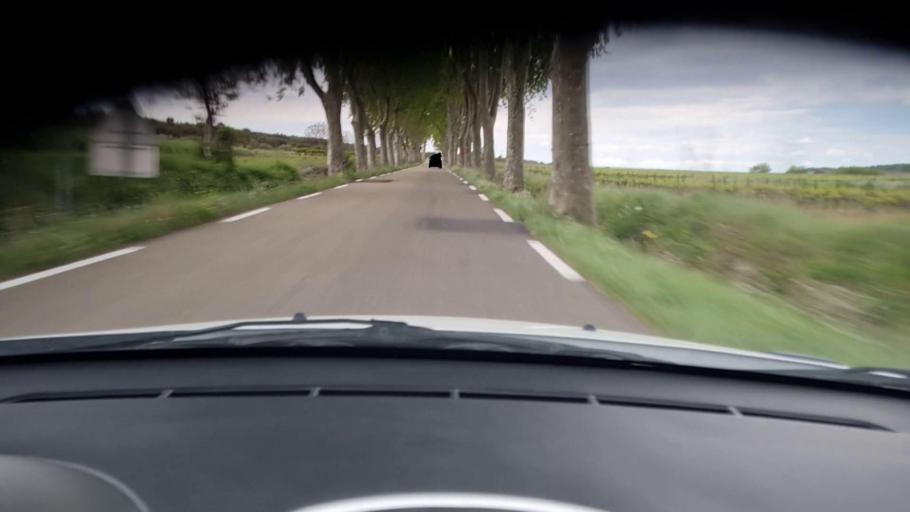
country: FR
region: Languedoc-Roussillon
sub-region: Departement du Gard
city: Uzes
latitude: 43.9794
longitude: 4.4066
